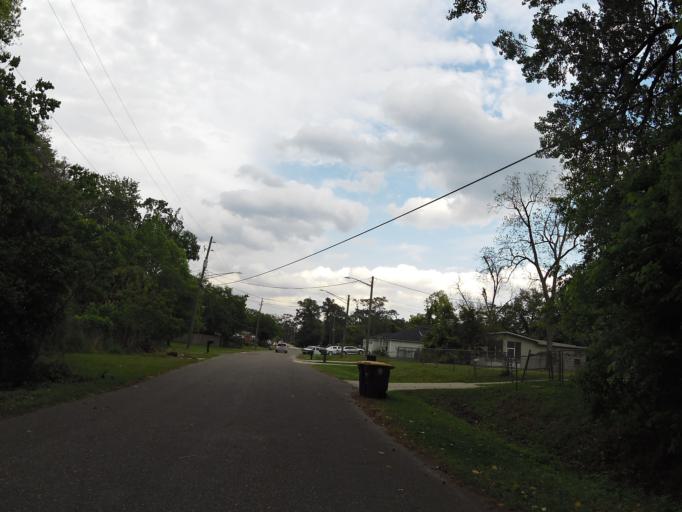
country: US
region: Florida
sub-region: Duval County
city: Jacksonville
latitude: 30.2939
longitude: -81.7324
